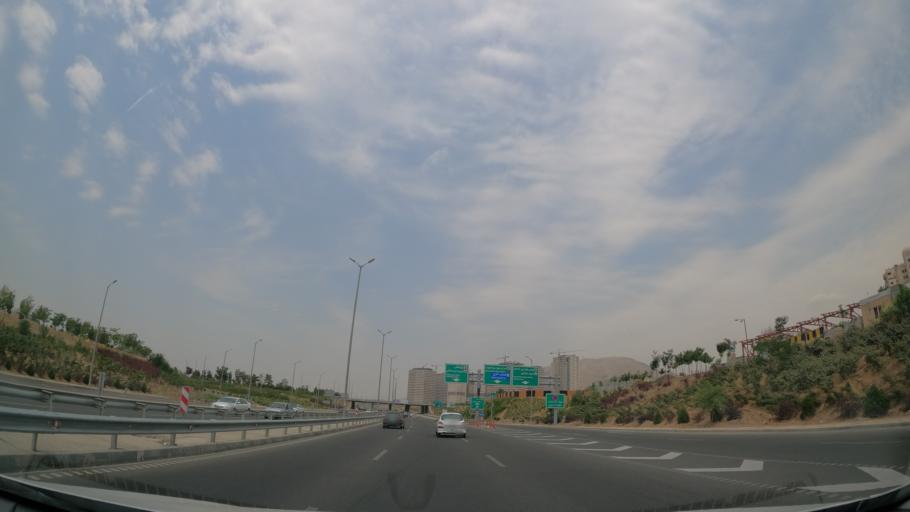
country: IR
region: Tehran
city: Shahr-e Qods
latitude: 35.7451
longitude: 51.1942
